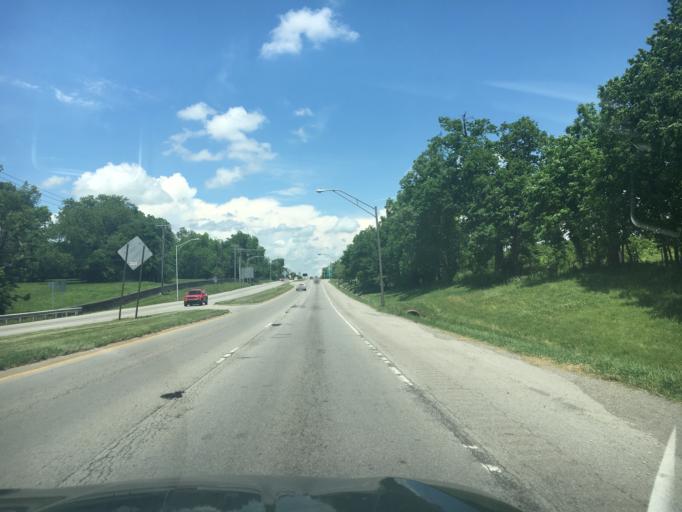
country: US
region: Kentucky
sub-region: Fayette County
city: Lexington-Fayette
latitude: 38.0802
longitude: -84.4927
